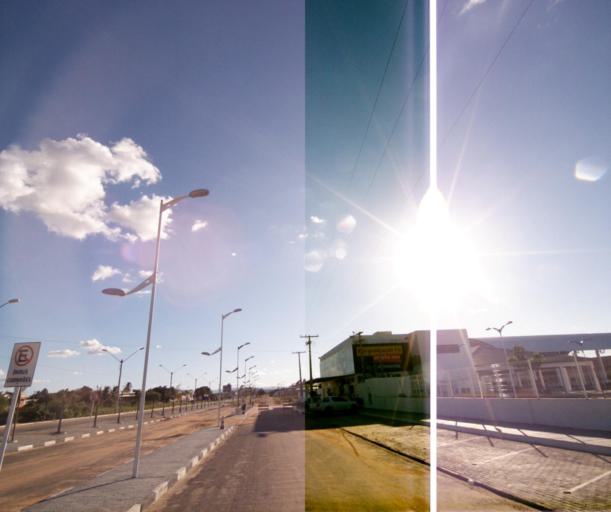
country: BR
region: Bahia
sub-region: Guanambi
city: Guanambi
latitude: -14.2044
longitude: -42.7597
